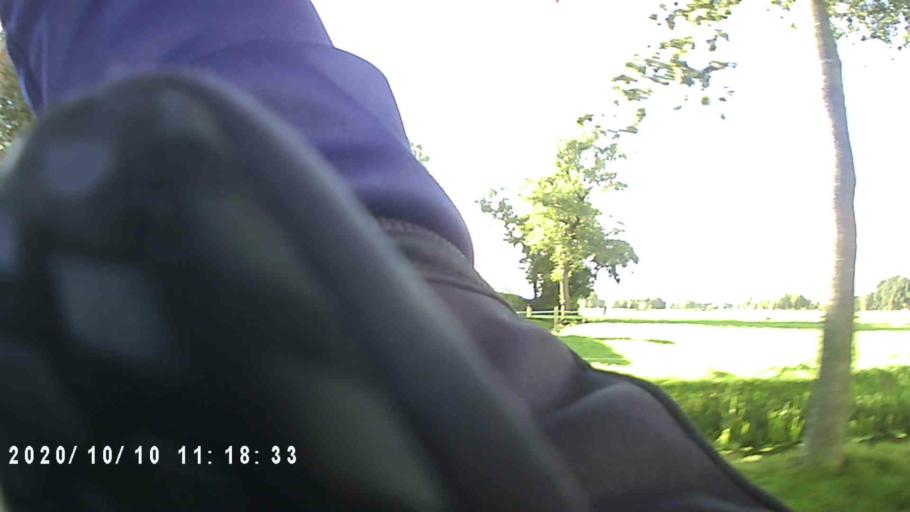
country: NL
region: Friesland
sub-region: Gemeente Smallingerland
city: Drachtstercompagnie
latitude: 53.0944
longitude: 6.1961
